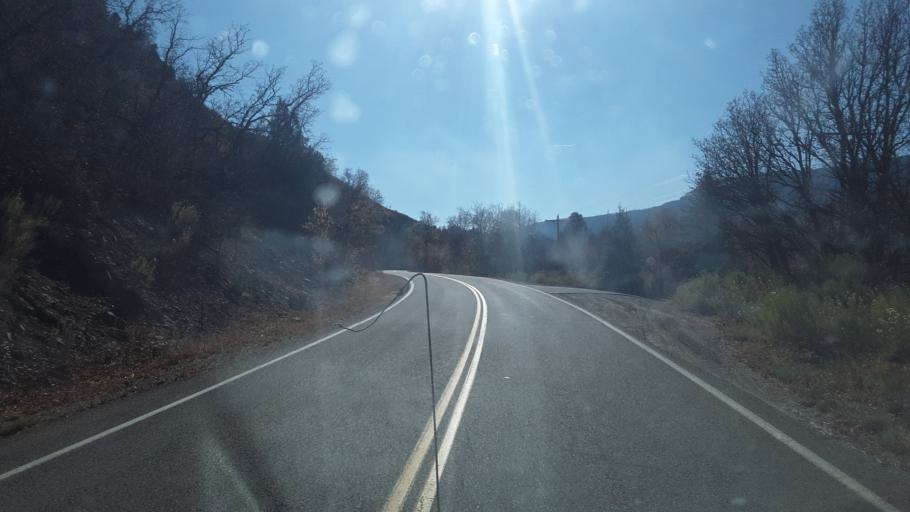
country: US
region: Colorado
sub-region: La Plata County
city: Durango
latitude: 37.3899
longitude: -107.8269
